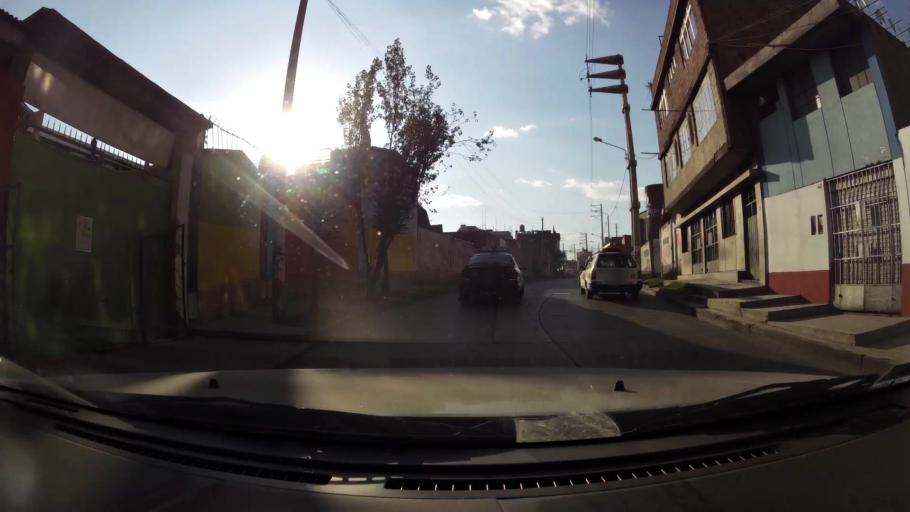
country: PE
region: Junin
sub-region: Provincia de Huancayo
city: El Tambo
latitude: -12.0549
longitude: -75.2166
